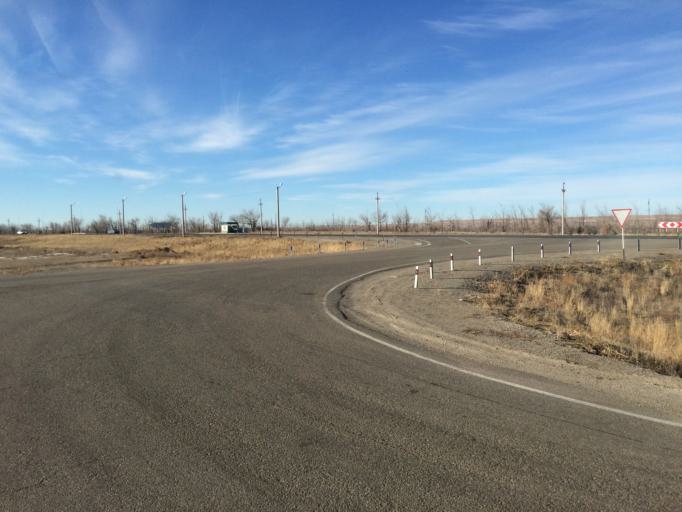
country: KZ
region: Aqtoebe
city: Aqtobe
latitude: 50.2636
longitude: 56.9536
